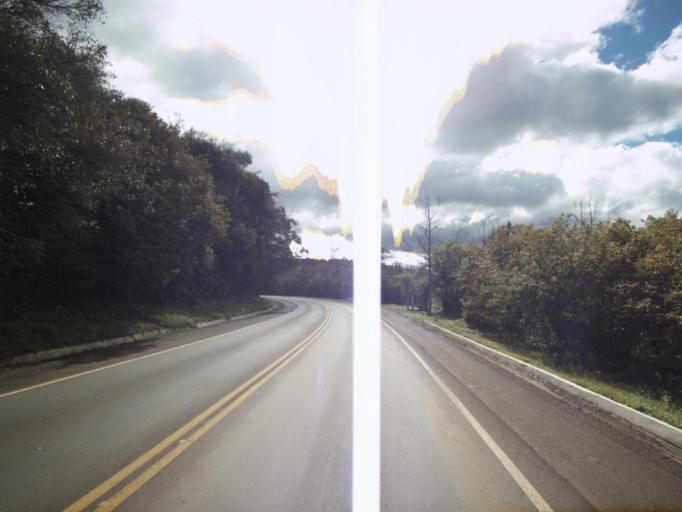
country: BR
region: Santa Catarina
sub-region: Concordia
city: Concordia
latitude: -27.3520
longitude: -51.9891
